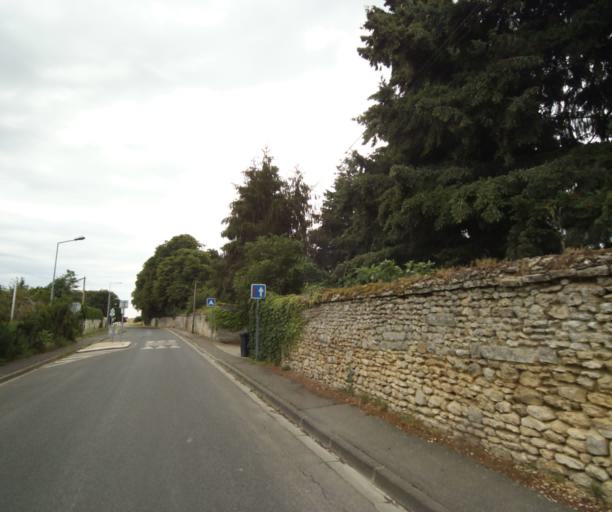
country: FR
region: Ile-de-France
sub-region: Departement de l'Essonne
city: Soisy-sur-Ecole
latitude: 48.4776
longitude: 2.5002
